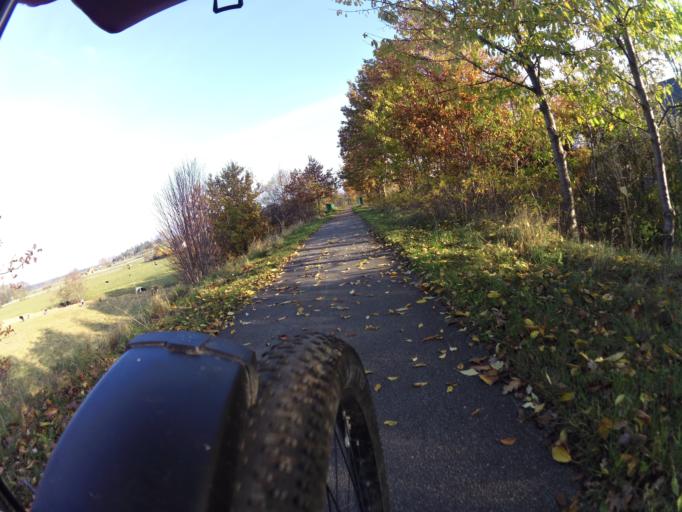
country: PL
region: Pomeranian Voivodeship
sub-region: Powiat pucki
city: Krokowa
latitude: 54.7822
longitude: 18.1675
